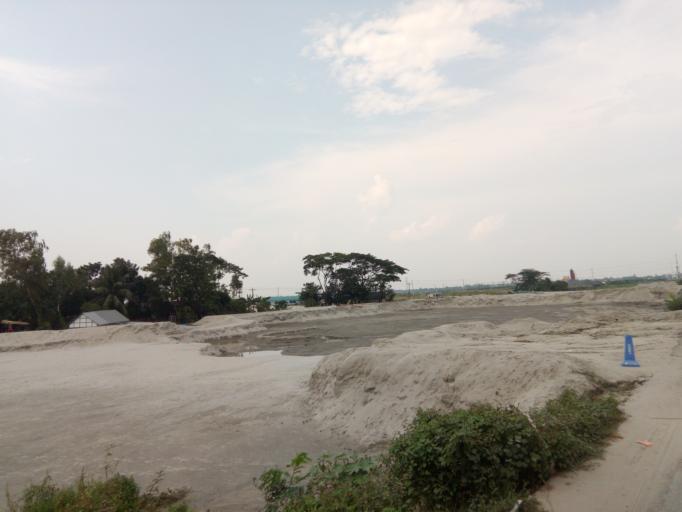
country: BD
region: Dhaka
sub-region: Dhaka
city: Dhaka
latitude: 23.6172
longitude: 90.3337
